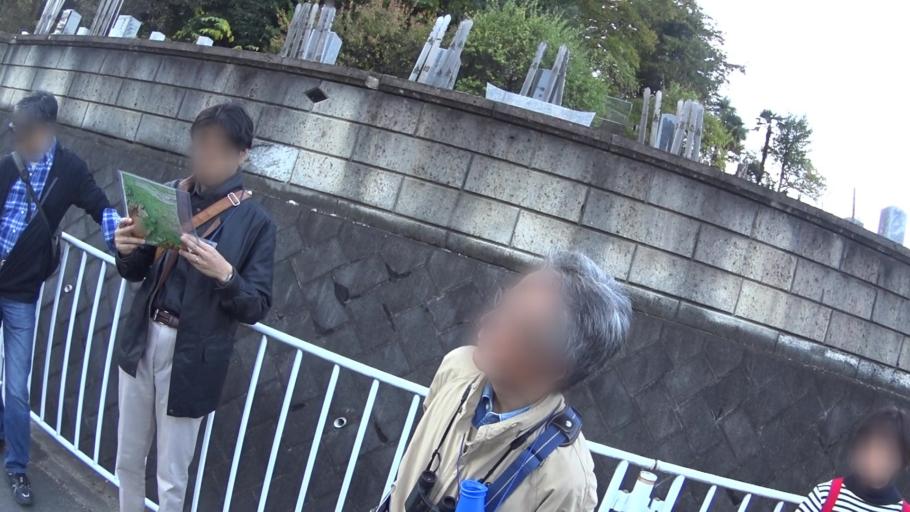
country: JP
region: Tokyo
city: Chofugaoka
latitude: 35.6325
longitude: 139.5149
